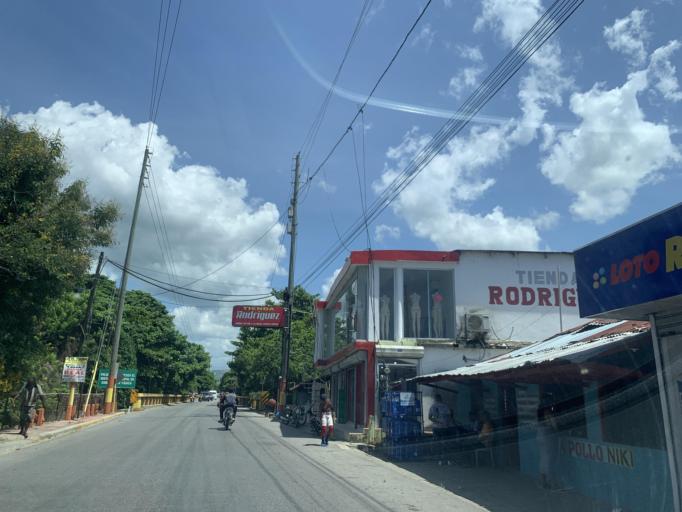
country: DO
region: Espaillat
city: Jamao al Norte
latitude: 19.6741
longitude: -70.3734
